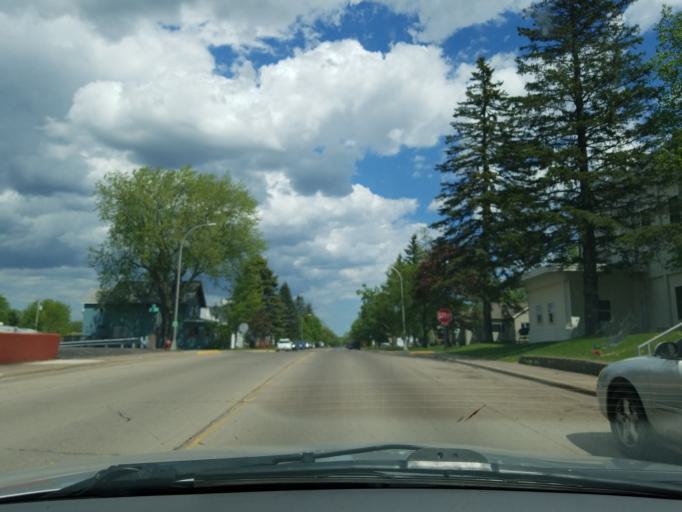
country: US
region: Minnesota
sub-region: Saint Louis County
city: Proctor
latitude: 46.7439
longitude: -92.2230
